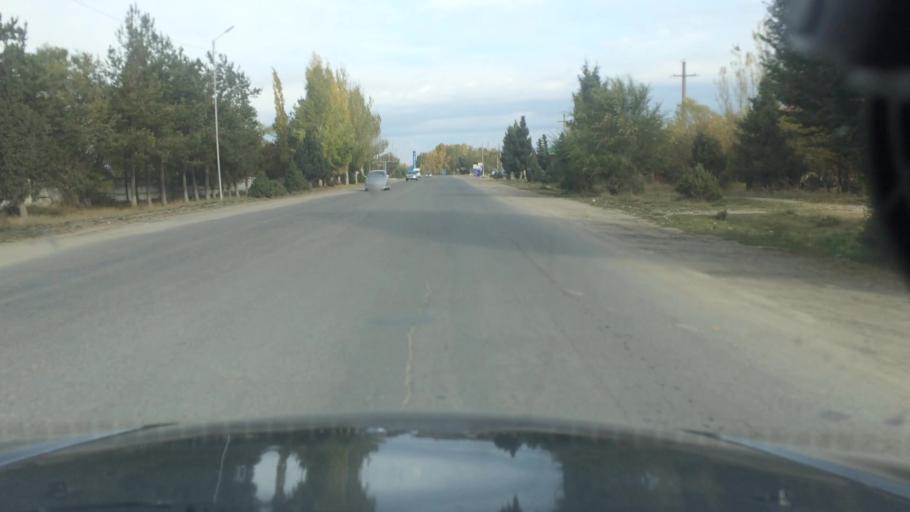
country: KG
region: Ysyk-Koel
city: Karakol
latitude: 42.5288
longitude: 78.3835
